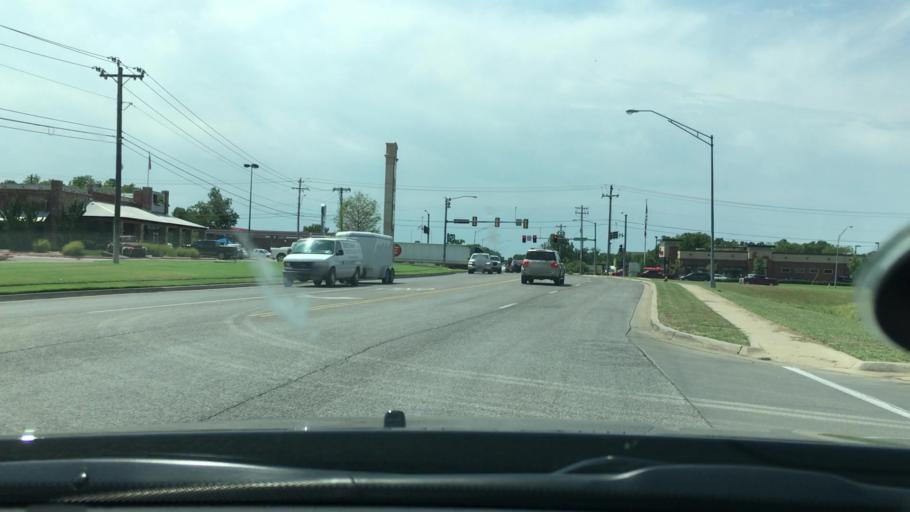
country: US
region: Oklahoma
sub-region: Carter County
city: Ardmore
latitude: 34.1888
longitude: -97.1606
